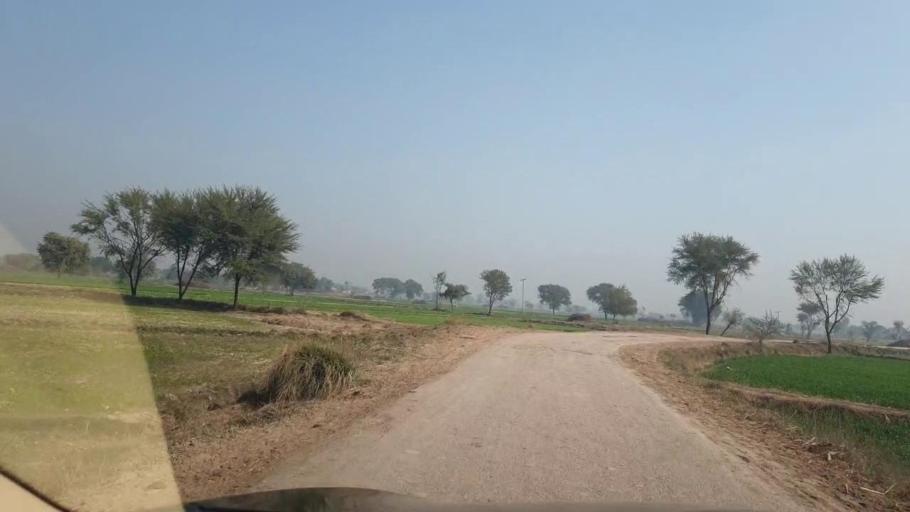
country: PK
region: Sindh
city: Ubauro
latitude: 28.1142
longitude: 69.7317
